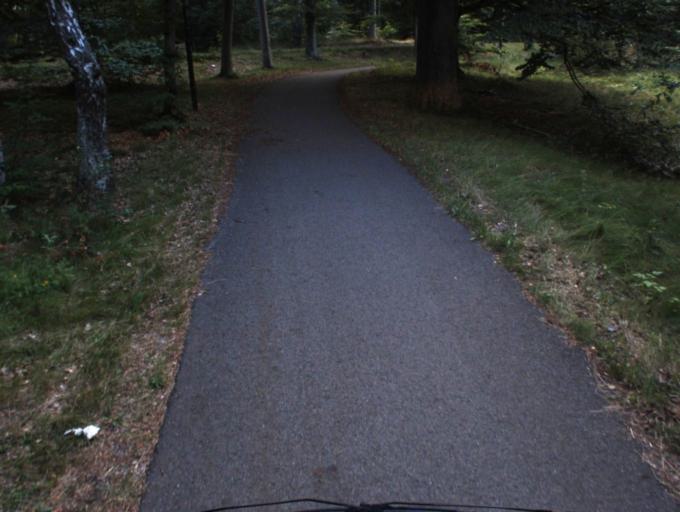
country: DK
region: Capital Region
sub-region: Helsingor Kommune
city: Hellebaek
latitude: 56.1126
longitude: 12.6180
